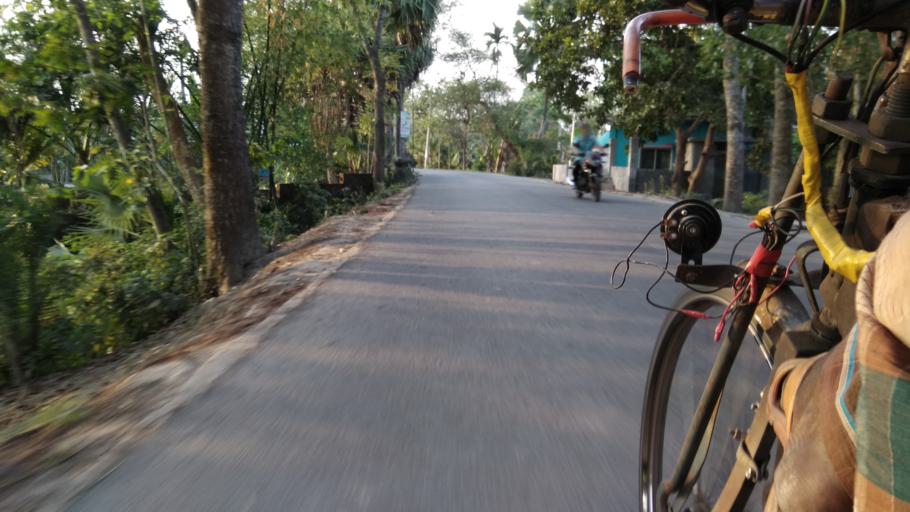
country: BD
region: Barisal
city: Mehendiganj
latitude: 22.9203
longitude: 90.4090
